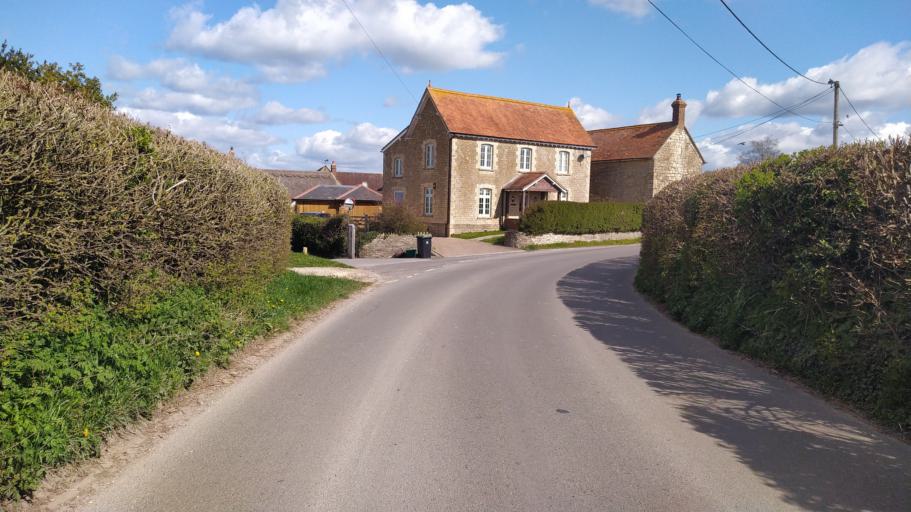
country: GB
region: England
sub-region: Dorset
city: Sturminster Newton
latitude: 50.9639
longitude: -2.3258
